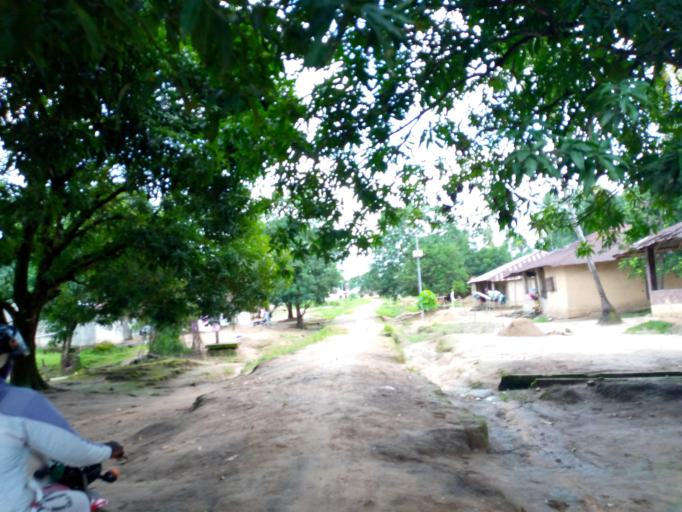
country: SL
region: Northern Province
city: Magburaka
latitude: 8.7195
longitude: -11.9574
